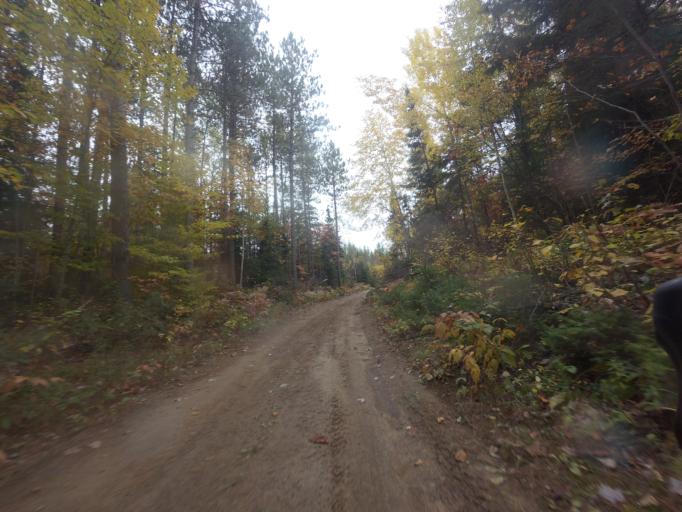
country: CA
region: Ontario
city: Petawawa
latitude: 45.7692
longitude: -77.3722
